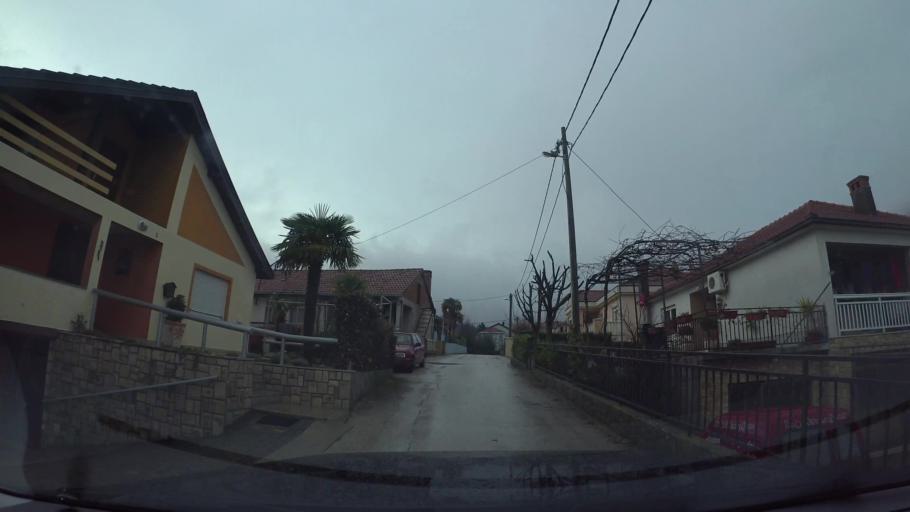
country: BA
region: Federation of Bosnia and Herzegovina
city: Cim
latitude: 43.3479
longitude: 17.7776
